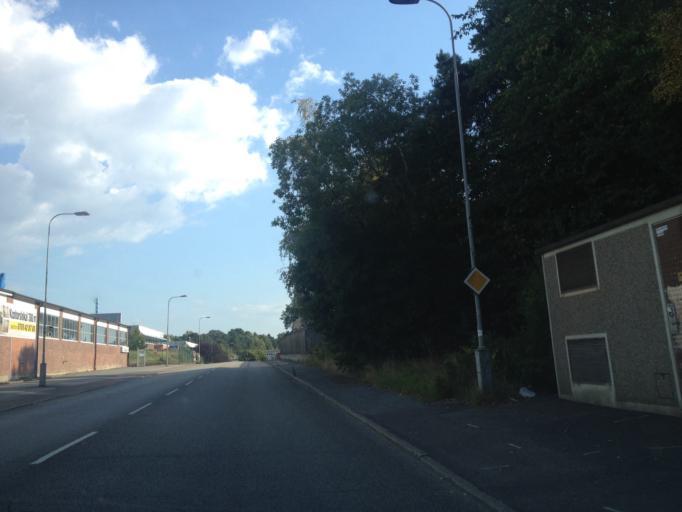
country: SE
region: Vaestra Goetaland
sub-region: Goteborg
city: Majorna
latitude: 57.6581
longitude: 11.9397
